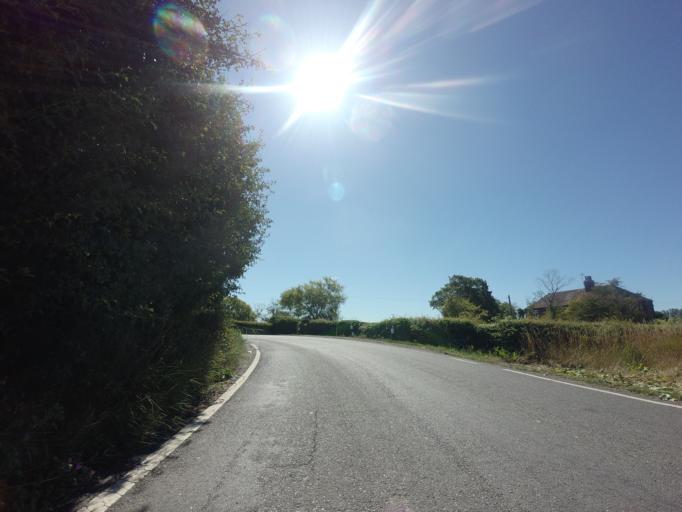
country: GB
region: England
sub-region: Kent
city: Ash
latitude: 51.3135
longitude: 1.2118
